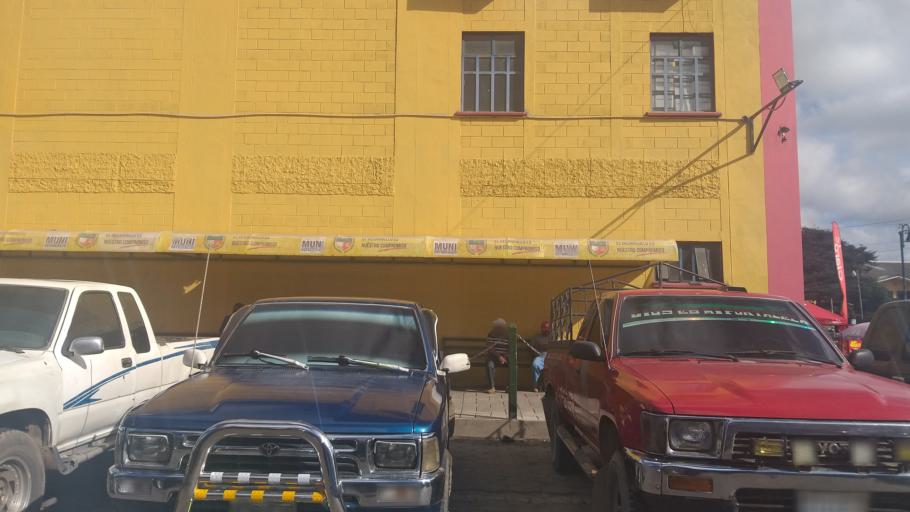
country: GT
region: Quetzaltenango
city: Ostuncalco
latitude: 14.8686
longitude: -91.6221
